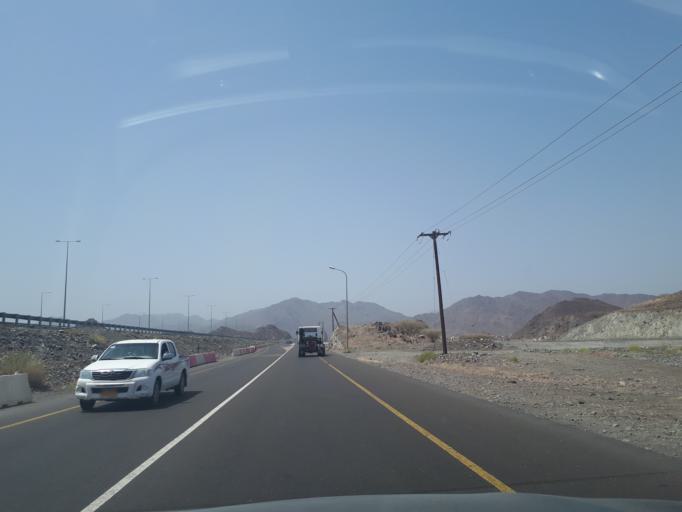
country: OM
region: Muhafazat ad Dakhiliyah
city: Sufalat Sama'il
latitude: 23.2856
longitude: 58.1083
